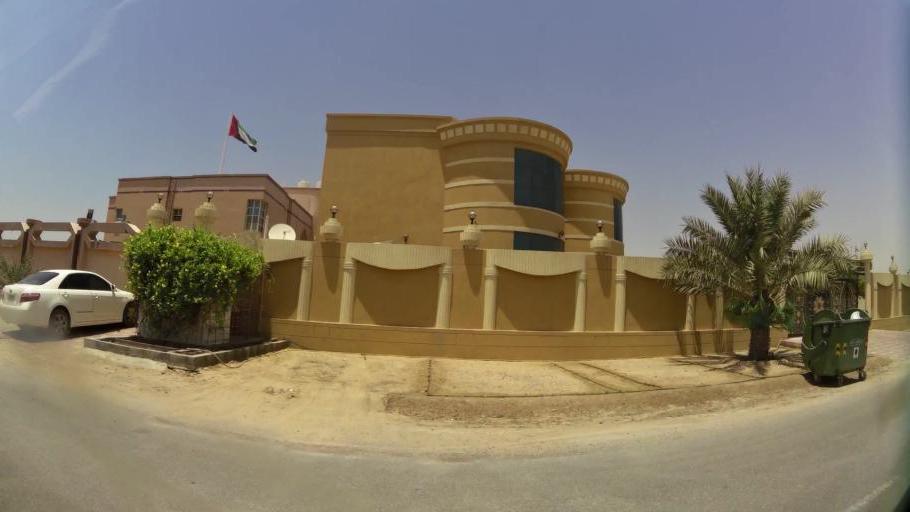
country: AE
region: Ajman
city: Ajman
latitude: 25.4103
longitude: 55.4989
